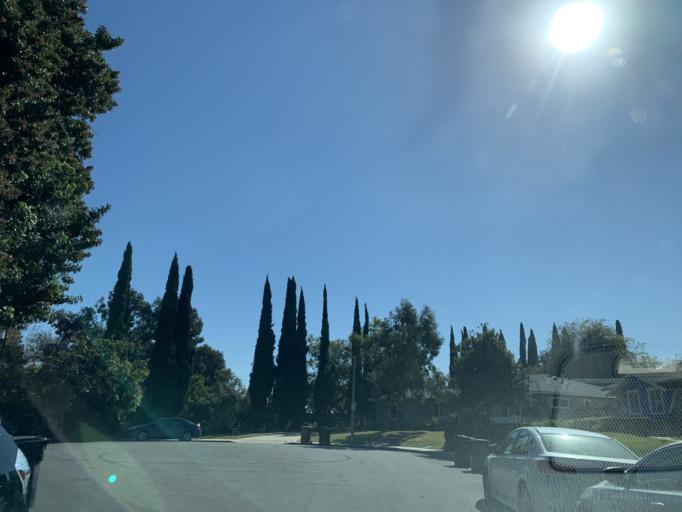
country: US
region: California
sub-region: Orange County
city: Placentia
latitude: 33.8811
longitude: -117.8975
